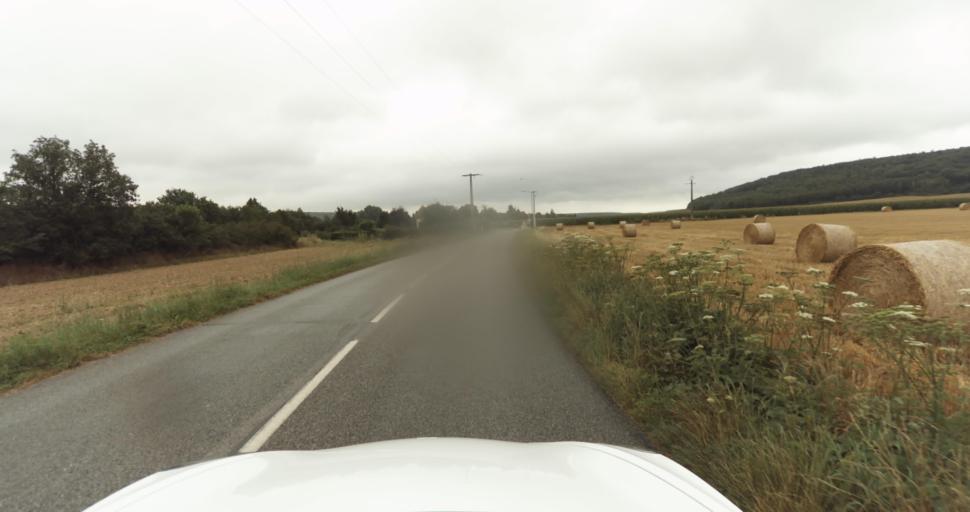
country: FR
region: Haute-Normandie
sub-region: Departement de l'Eure
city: Normanville
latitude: 49.0786
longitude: 1.1465
